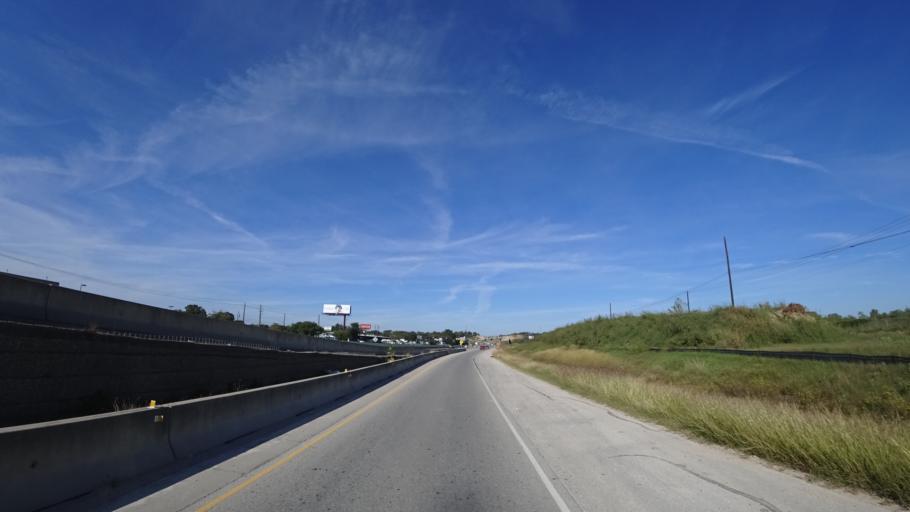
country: US
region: Texas
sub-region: Travis County
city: Austin
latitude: 30.2558
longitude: -97.6773
